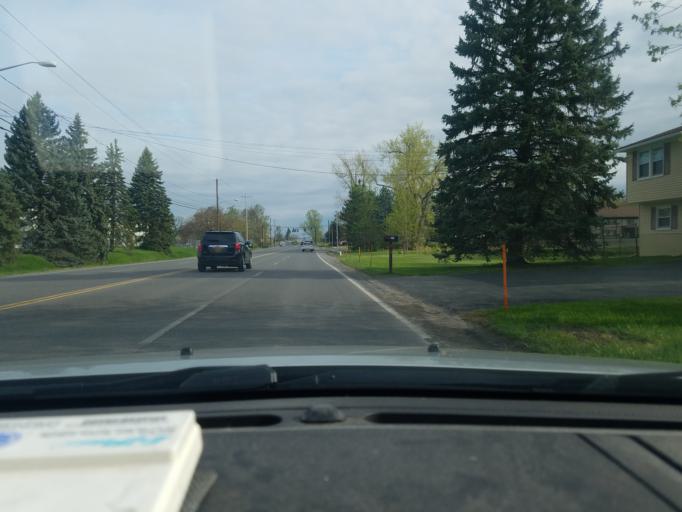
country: US
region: New York
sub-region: Onondaga County
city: East Syracuse
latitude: 43.0836
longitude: -76.0779
